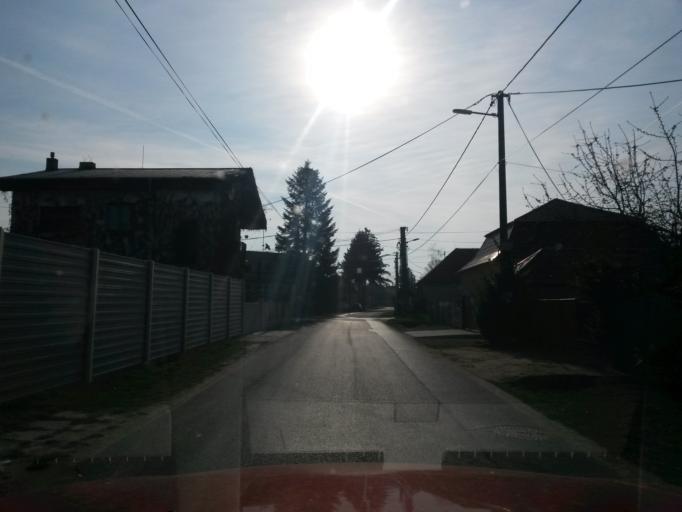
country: SK
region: Nitriansky
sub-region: Okres Komarno
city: Hurbanovo
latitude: 47.8837
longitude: 18.2020
